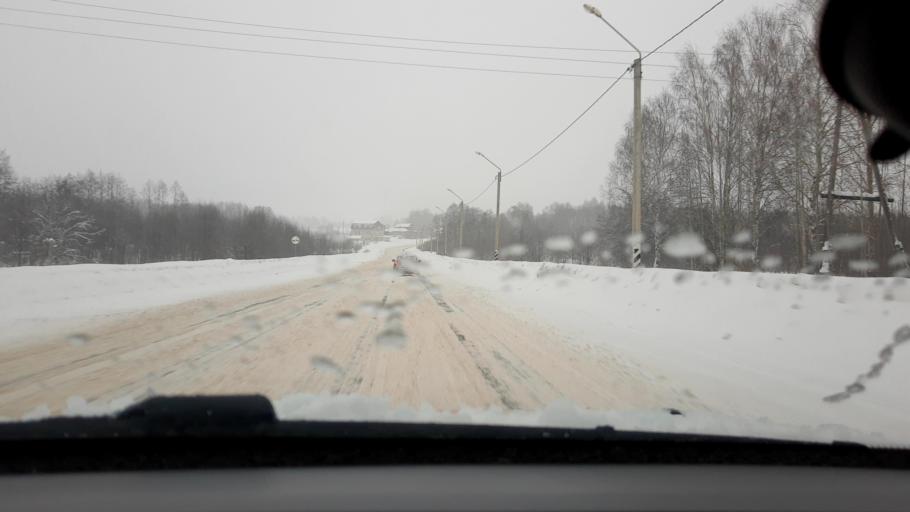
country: RU
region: Nizjnij Novgorod
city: Purekh
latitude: 56.6519
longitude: 43.0841
